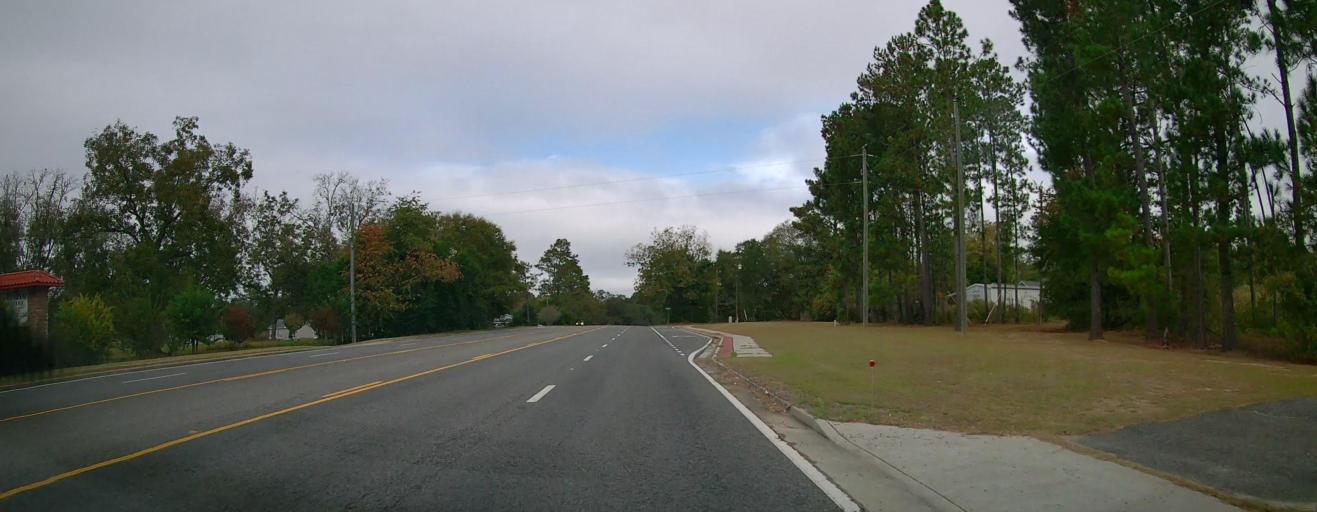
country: US
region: Georgia
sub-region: Tift County
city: Unionville
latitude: 31.4343
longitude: -83.5347
